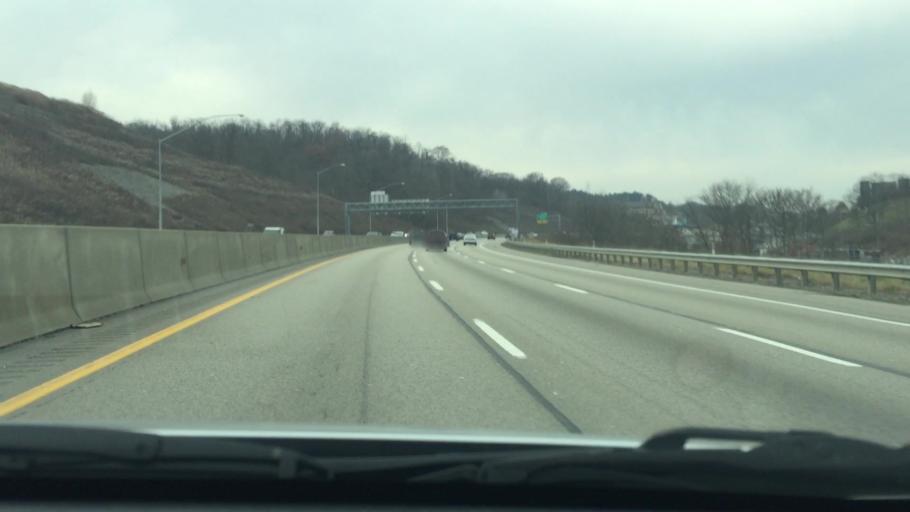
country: US
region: Pennsylvania
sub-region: Allegheny County
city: Rennerdale
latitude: 40.4250
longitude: -80.1199
